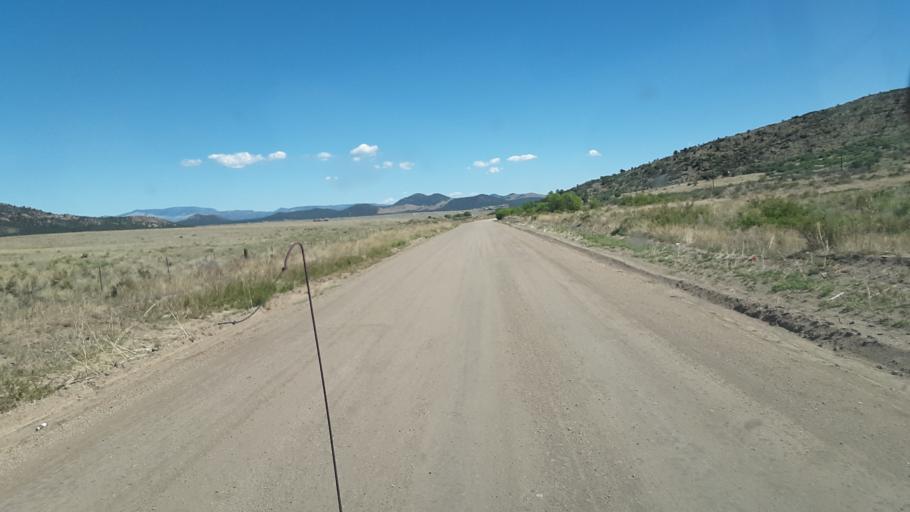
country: US
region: Colorado
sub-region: Custer County
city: Westcliffe
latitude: 38.2376
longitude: -105.5021
